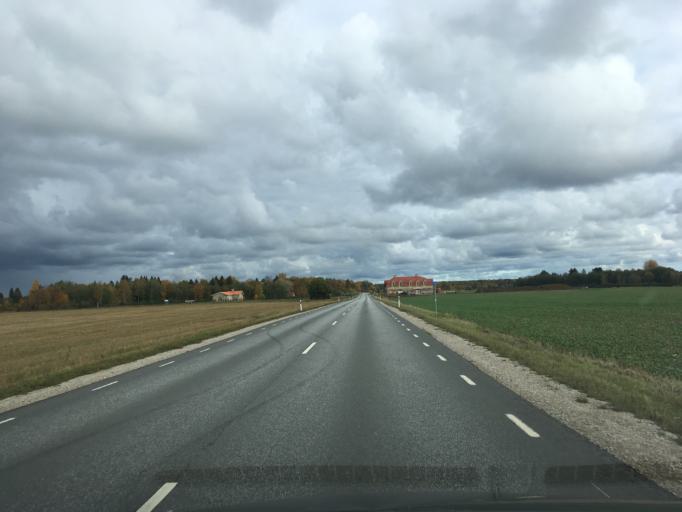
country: EE
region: Harju
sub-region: Anija vald
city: Kehra
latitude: 59.2766
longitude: 25.3645
